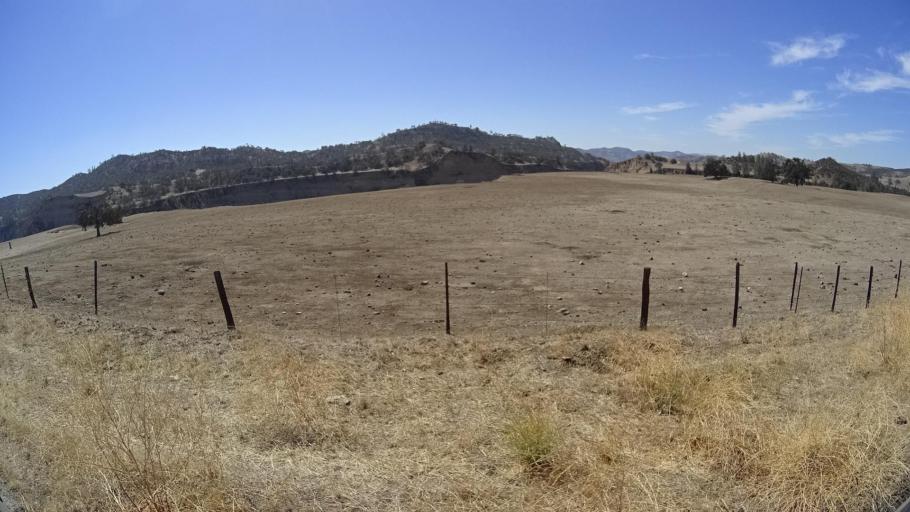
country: US
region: California
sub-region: Fresno County
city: Coalinga
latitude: 36.1000
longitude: -120.6957
